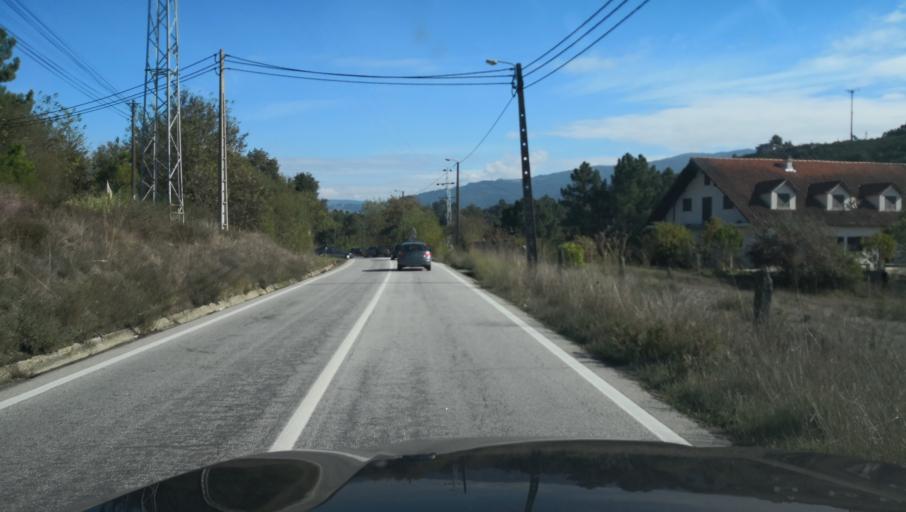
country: PT
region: Vila Real
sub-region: Chaves
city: Chaves
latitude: 41.7204
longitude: -7.4921
